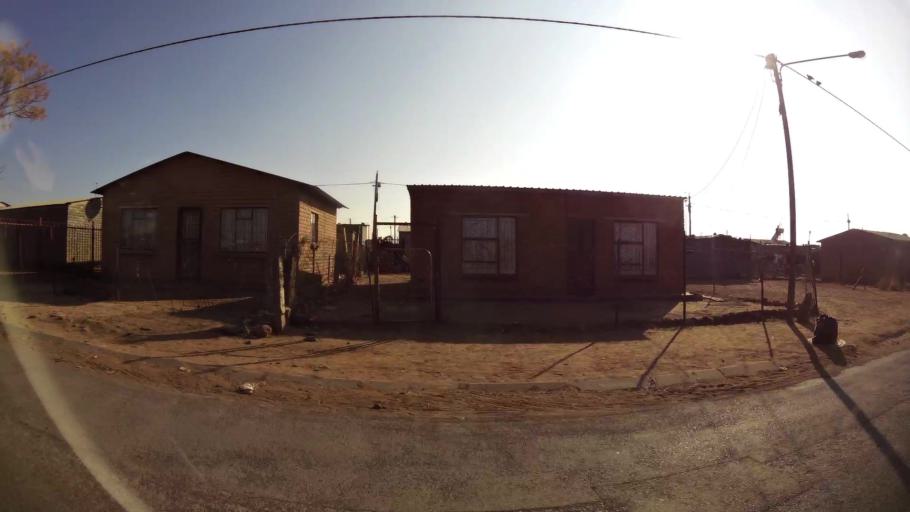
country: ZA
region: Orange Free State
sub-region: Mangaung Metropolitan Municipality
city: Bloemfontein
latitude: -29.2044
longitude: 26.2446
